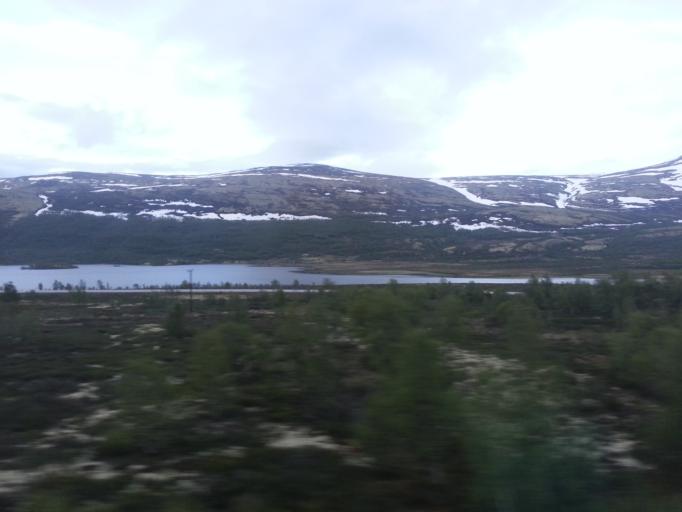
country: NO
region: Oppland
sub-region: Dovre
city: Dovre
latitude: 62.1778
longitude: 9.4560
